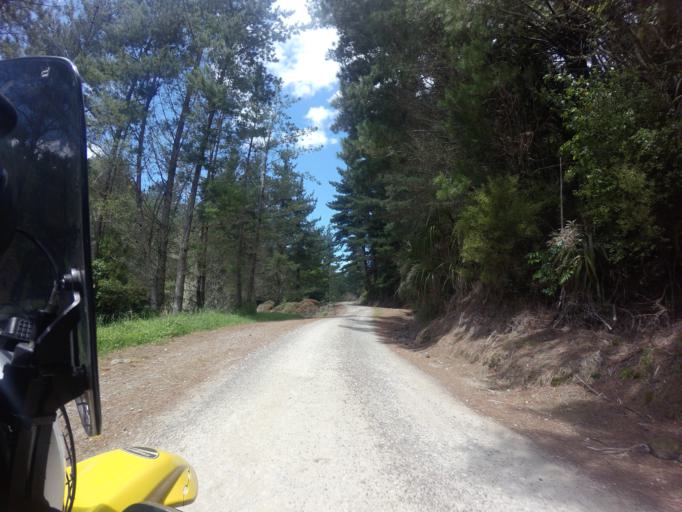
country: NZ
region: Hawke's Bay
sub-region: Wairoa District
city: Wairoa
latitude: -38.9729
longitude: 177.6870
